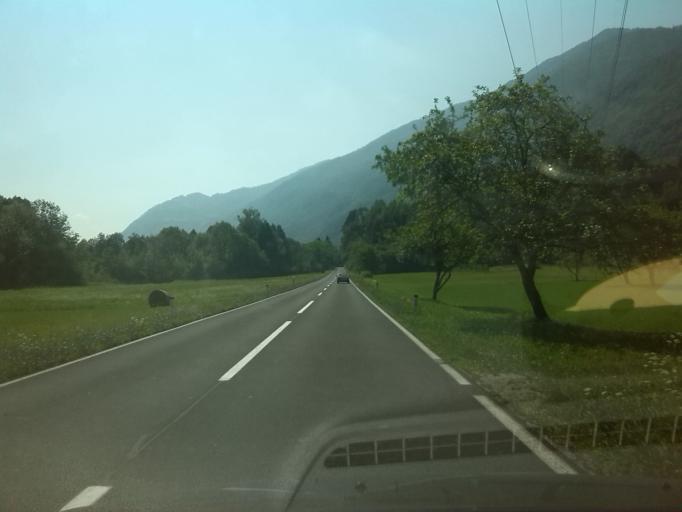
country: SI
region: Kobarid
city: Kobarid
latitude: 46.2239
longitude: 13.6023
